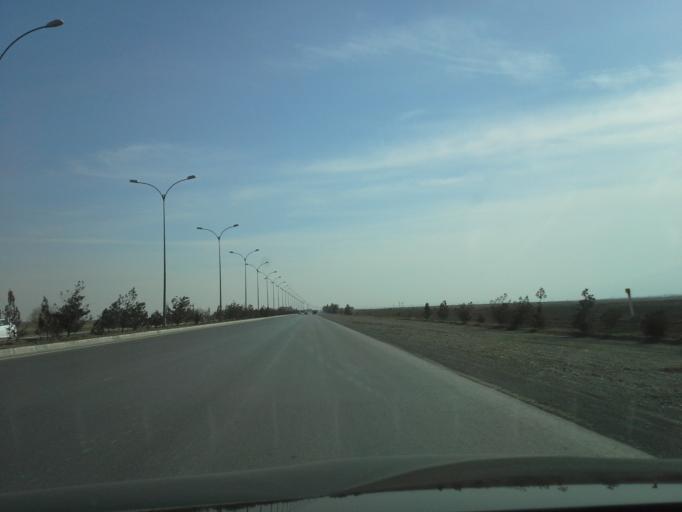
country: TM
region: Ahal
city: Abadan
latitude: 38.1290
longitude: 58.0260
